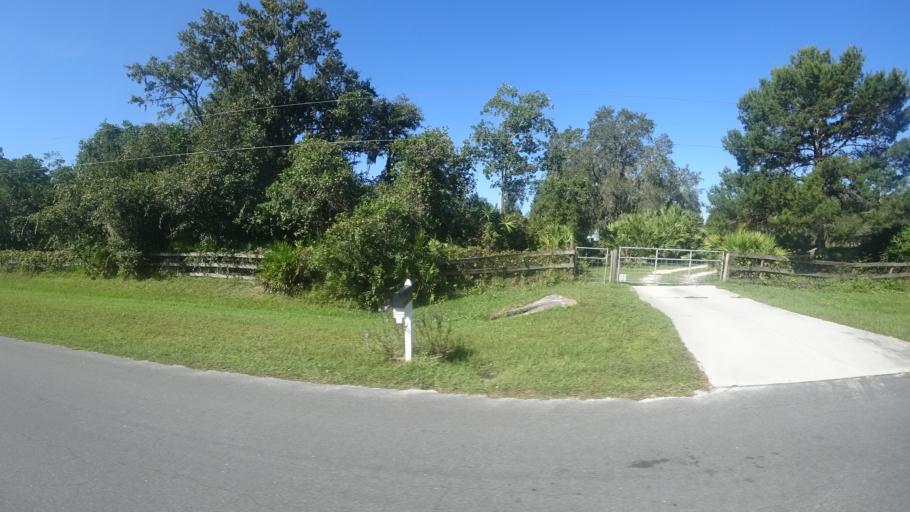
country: US
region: Florida
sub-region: Sarasota County
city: Lake Sarasota
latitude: 27.3537
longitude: -82.2509
